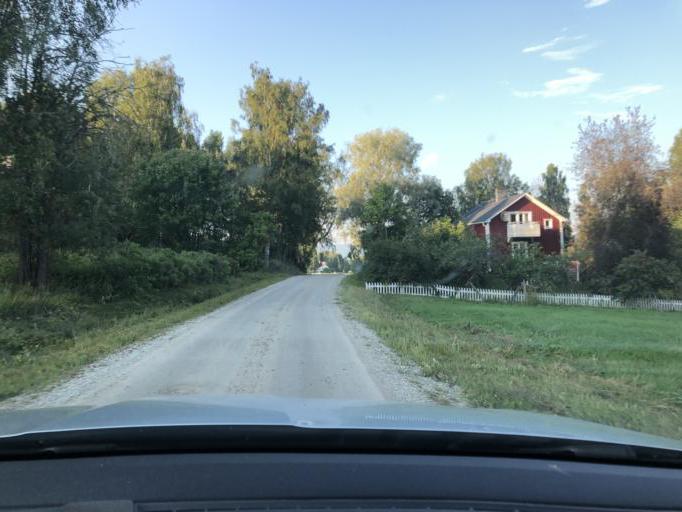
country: SE
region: Vaesternorrland
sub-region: Kramfors Kommun
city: Bollstabruk
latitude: 63.0526
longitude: 17.7250
